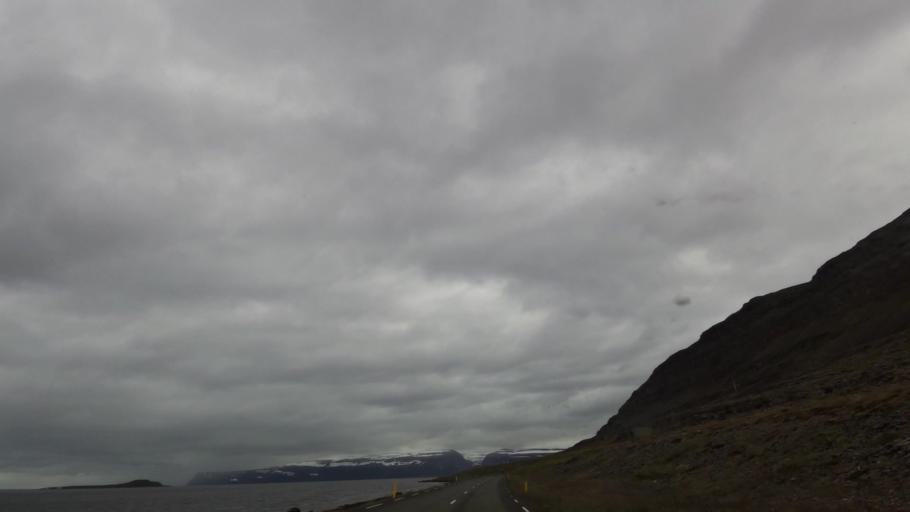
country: IS
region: Westfjords
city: Isafjoerdur
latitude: 66.0163
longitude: -22.7814
